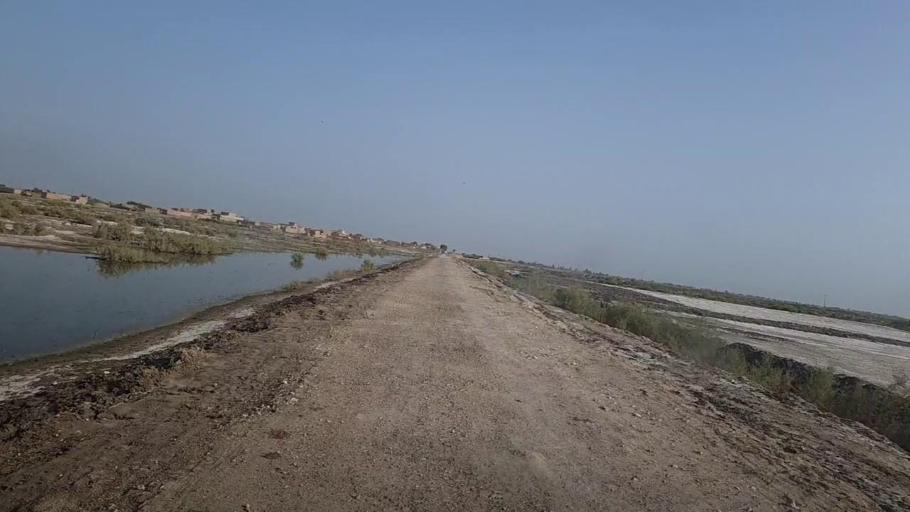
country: PK
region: Sindh
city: Sita Road
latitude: 27.1152
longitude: 67.8813
